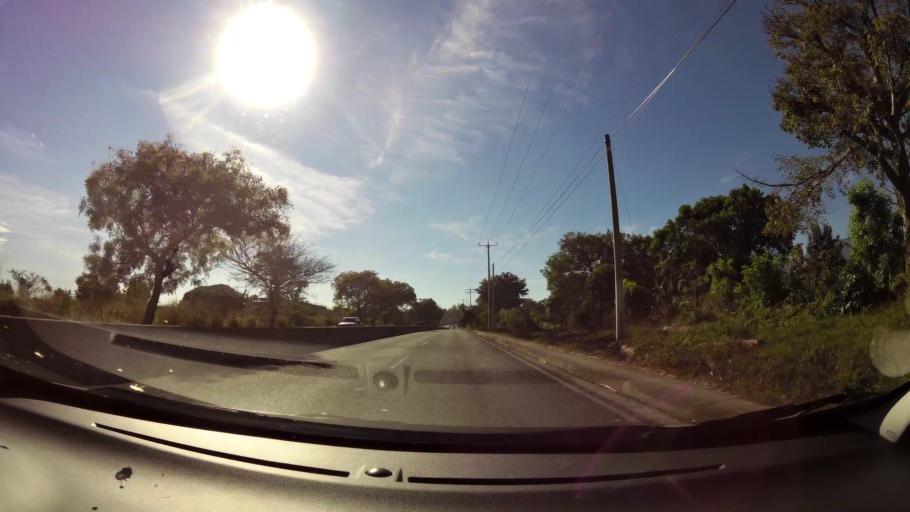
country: SV
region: Santa Ana
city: Santa Ana
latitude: 13.9637
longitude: -89.5800
